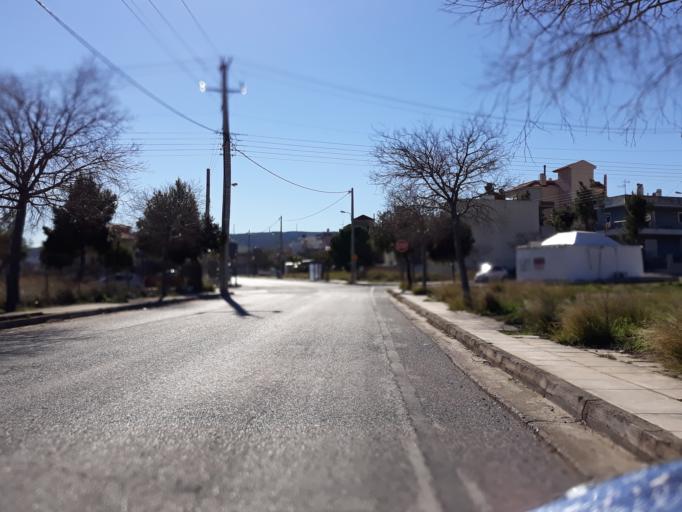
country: GR
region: Attica
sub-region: Nomarchia Dytikis Attikis
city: Ano Liosia
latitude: 38.0908
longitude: 23.7100
